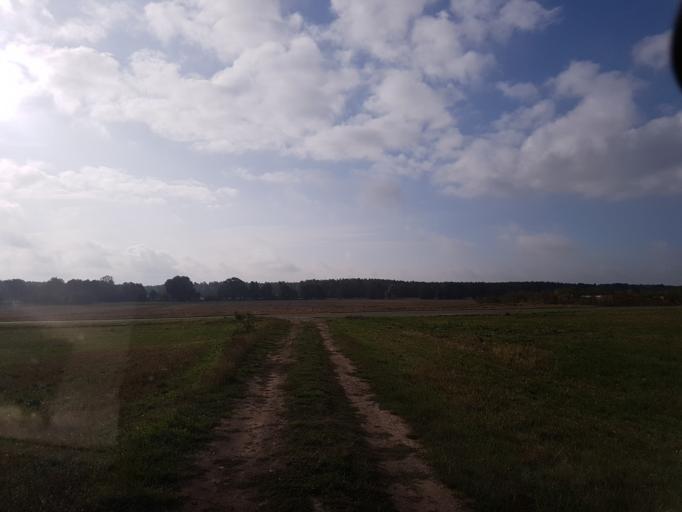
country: DE
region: Brandenburg
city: Finsterwalde
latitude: 51.6249
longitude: 13.7666
